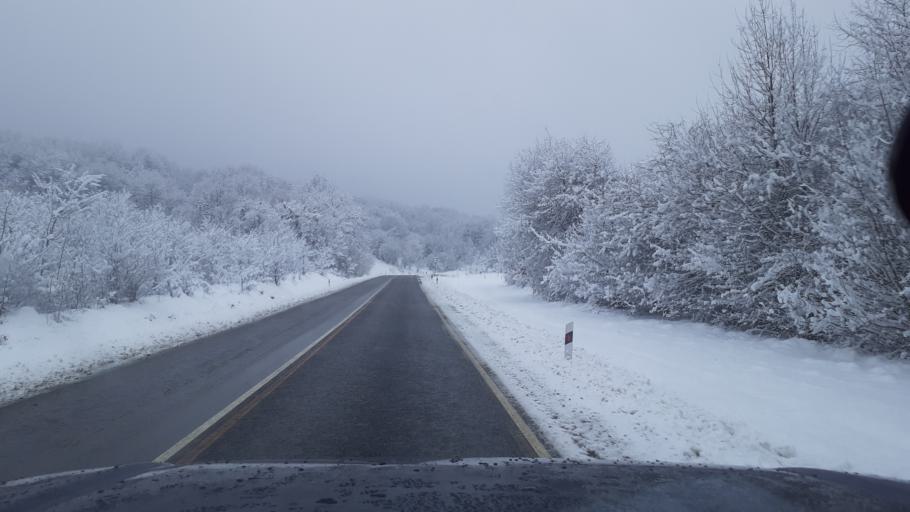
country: RU
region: Adygeya
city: Kamennomostskiy
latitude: 44.2101
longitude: 40.1980
